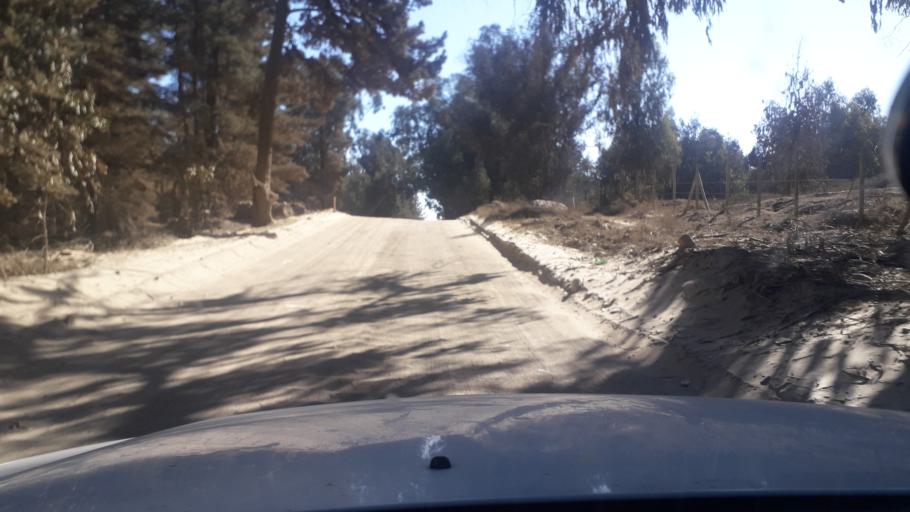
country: CL
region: Valparaiso
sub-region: Provincia de Valparaiso
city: Vina del Mar
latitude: -32.9551
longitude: -71.5247
